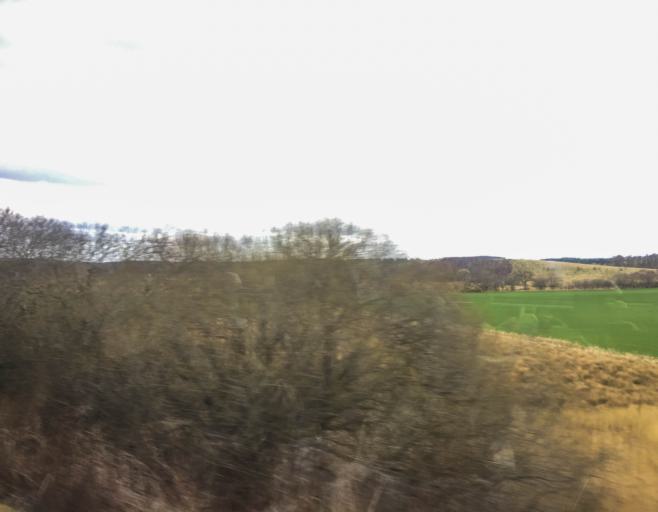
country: GB
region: Scotland
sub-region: South Lanarkshire
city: Law
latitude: 55.7454
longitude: -3.8624
